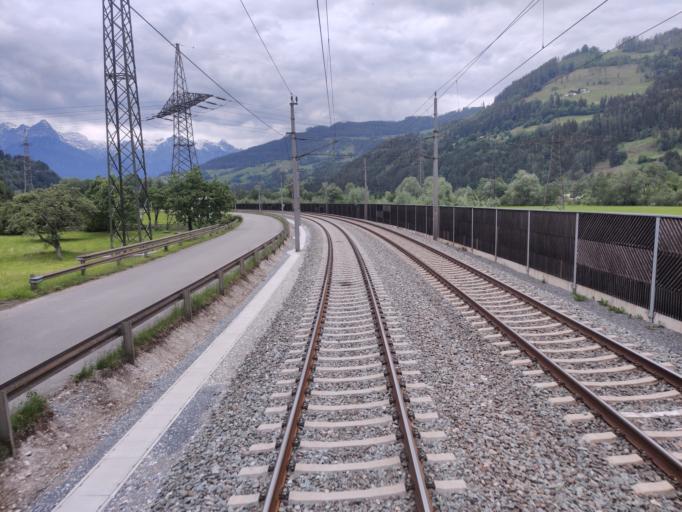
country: AT
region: Salzburg
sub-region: Politischer Bezirk Sankt Johann im Pongau
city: Sankt Johann im Pongau
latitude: 47.3778
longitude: 13.2109
